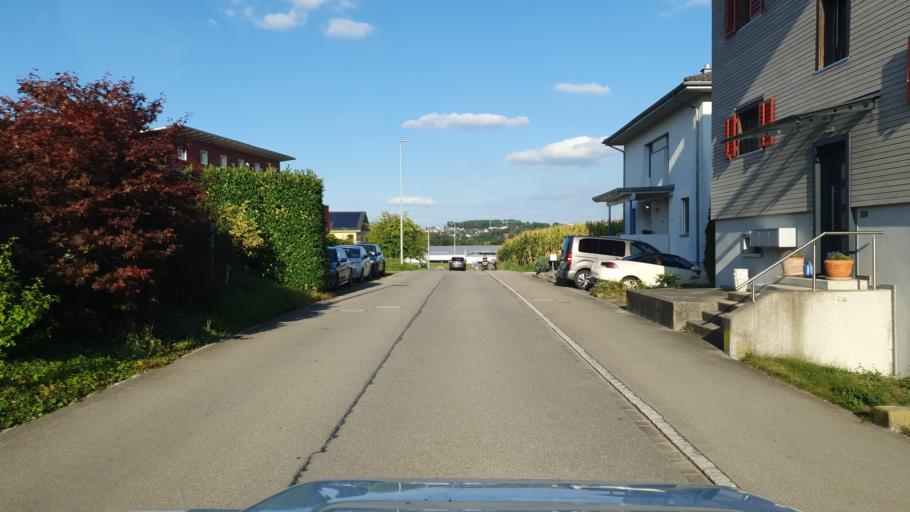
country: CH
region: Aargau
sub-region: Bezirk Muri
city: Oberruti
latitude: 47.1672
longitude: 8.3991
